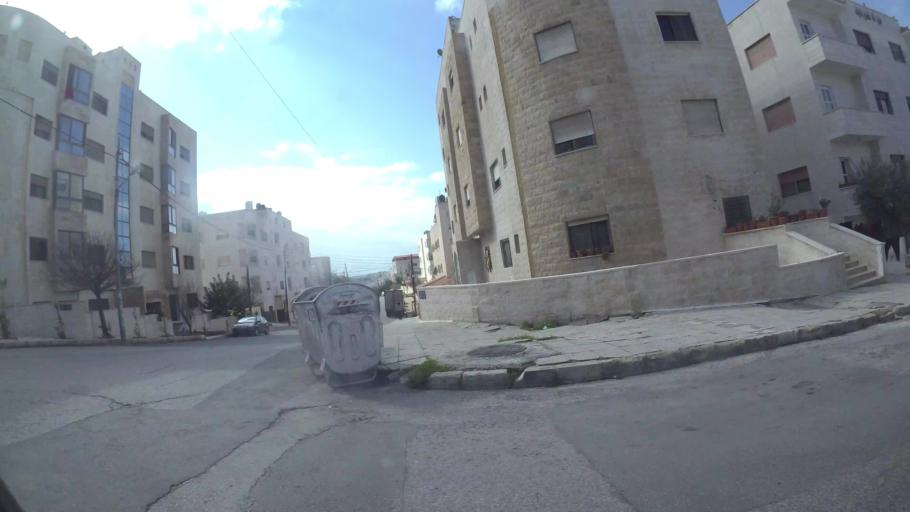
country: JO
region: Amman
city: Al Jubayhah
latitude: 32.0233
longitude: 35.8545
